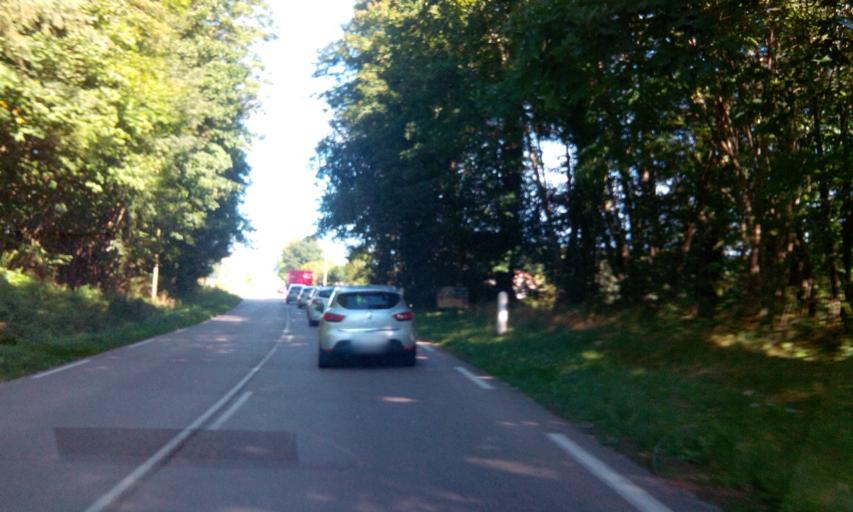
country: FR
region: Limousin
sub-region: Departement de la Haute-Vienne
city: Saint-Leonard-de-Noblat
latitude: 45.8405
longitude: 1.4661
